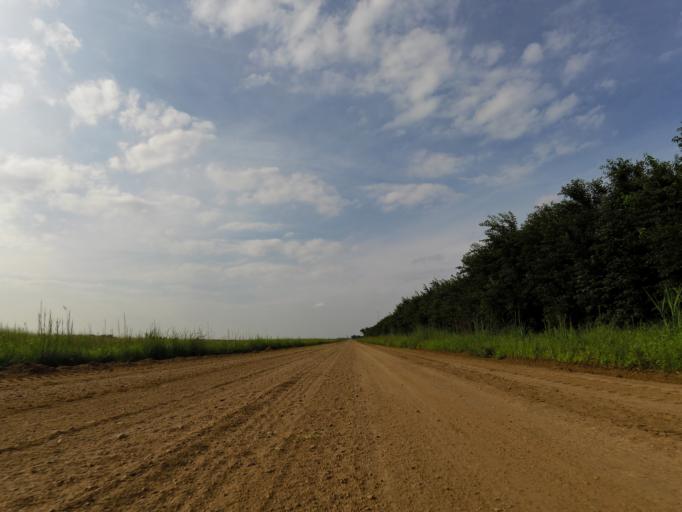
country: US
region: Kansas
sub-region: Reno County
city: South Hutchinson
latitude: 37.9600
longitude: -98.0689
